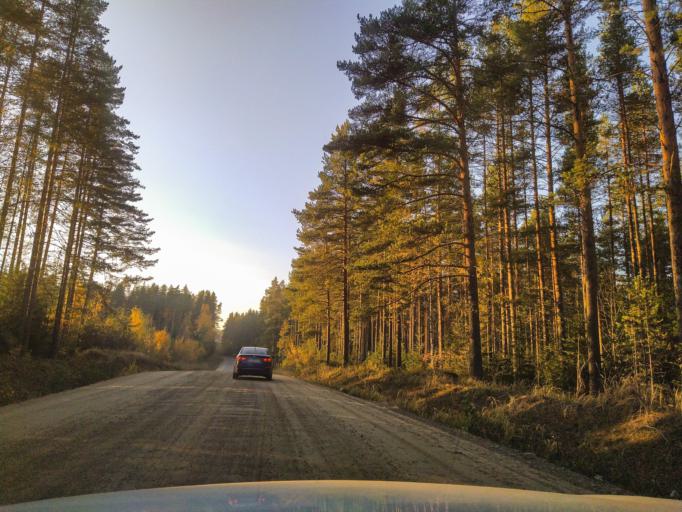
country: RU
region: Leningrad
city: Kuznechnoye
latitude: 61.3280
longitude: 29.9842
